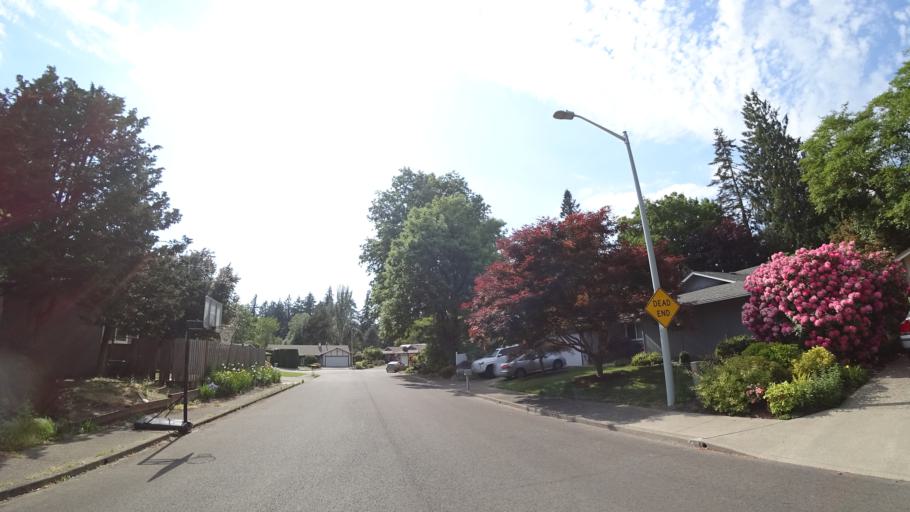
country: US
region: Oregon
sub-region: Washington County
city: Garden Home-Whitford
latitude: 45.4575
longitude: -122.7538
